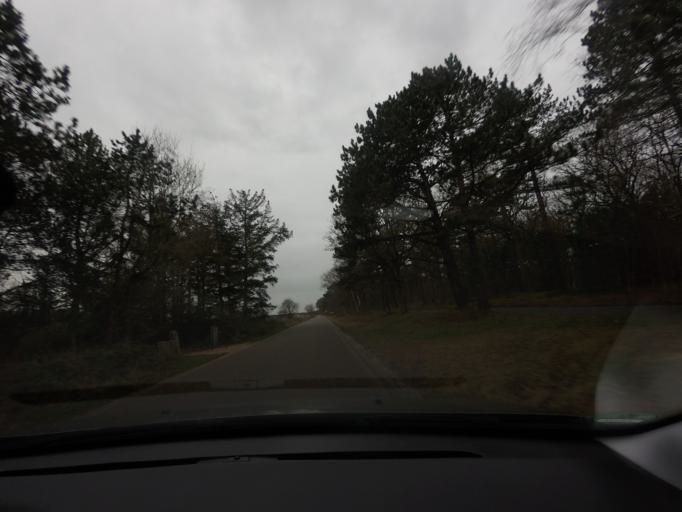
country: NL
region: North Holland
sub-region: Gemeente Texel
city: Den Burg
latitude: 53.0856
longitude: 4.7530
